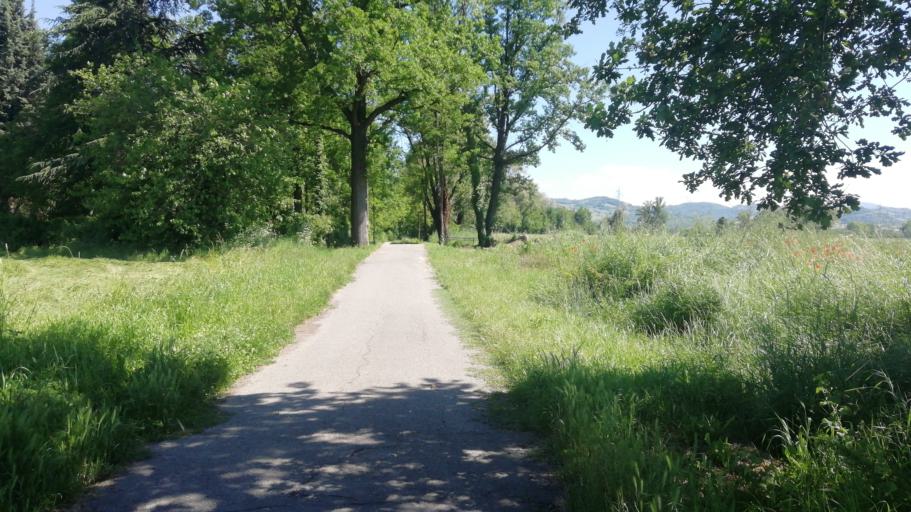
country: IT
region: Emilia-Romagna
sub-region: Provincia di Piacenza
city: Borgonovo Valtidone
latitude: 44.9936
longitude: 9.4563
